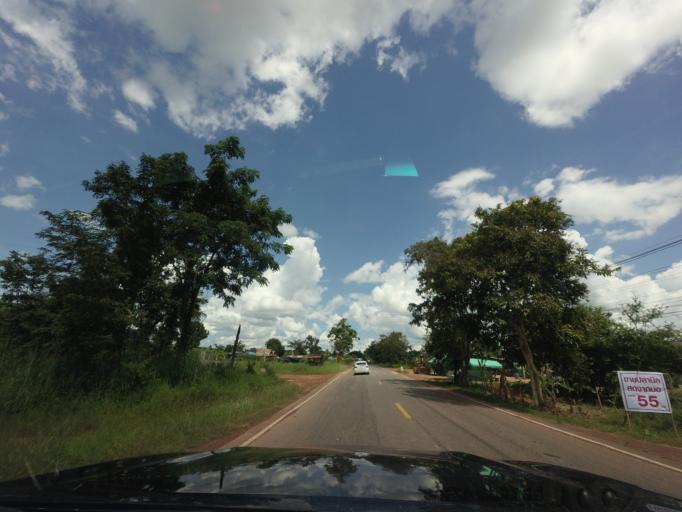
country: TH
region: Changwat Udon Thani
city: Phibun Rak
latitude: 17.6526
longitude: 103.1370
